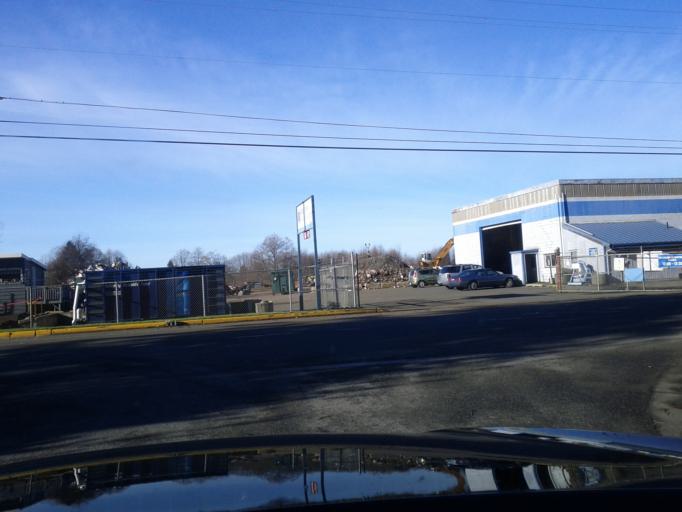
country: US
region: Washington
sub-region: Skagit County
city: Burlington
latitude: 48.4612
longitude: -122.3246
